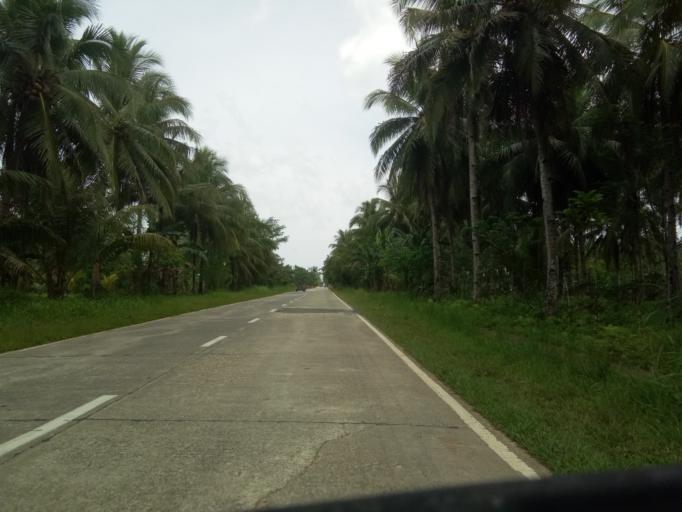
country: PH
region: Caraga
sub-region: Province of Surigao del Norte
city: San Isidro
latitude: 9.9231
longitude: 126.0508
